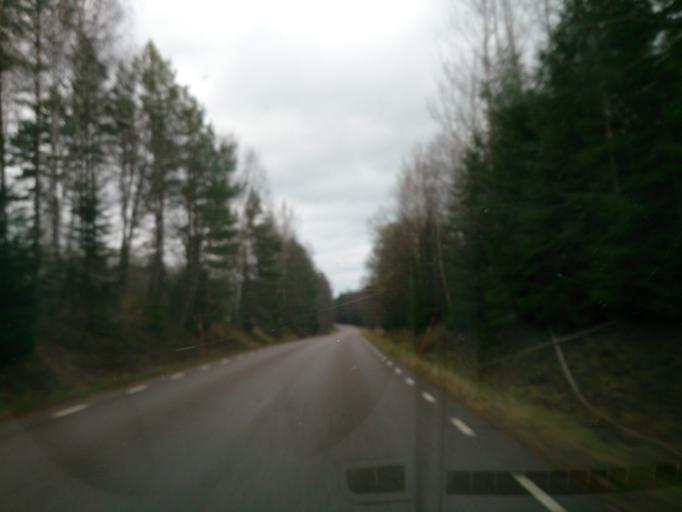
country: SE
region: OEstergoetland
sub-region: Atvidabergs Kommun
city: Atvidaberg
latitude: 58.2544
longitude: 16.0210
